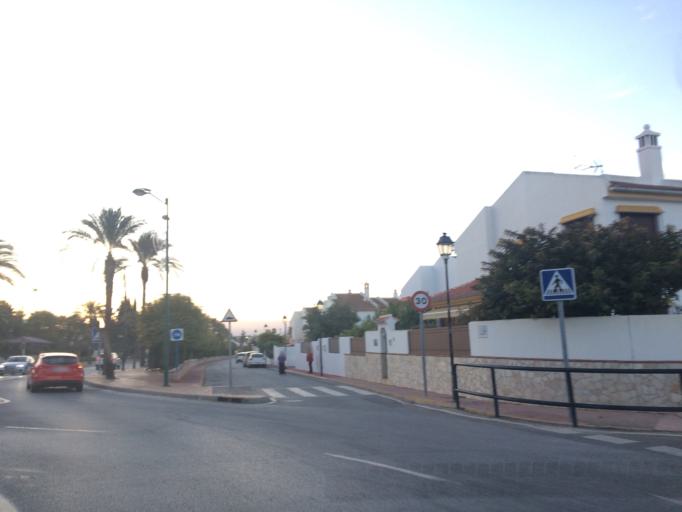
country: ES
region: Andalusia
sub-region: Provincia de Malaga
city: Alhaurin de la Torre
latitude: 36.6608
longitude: -4.5339
